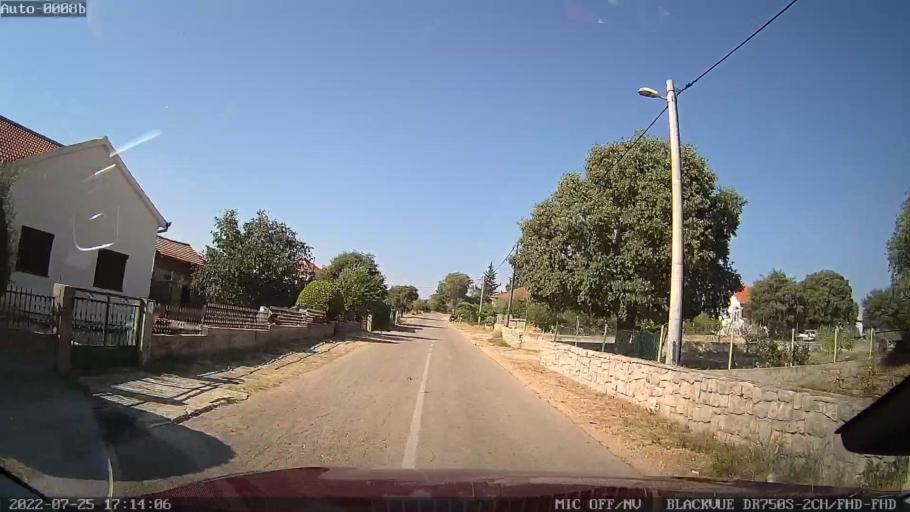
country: HR
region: Zadarska
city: Polaca
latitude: 44.0491
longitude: 15.5382
